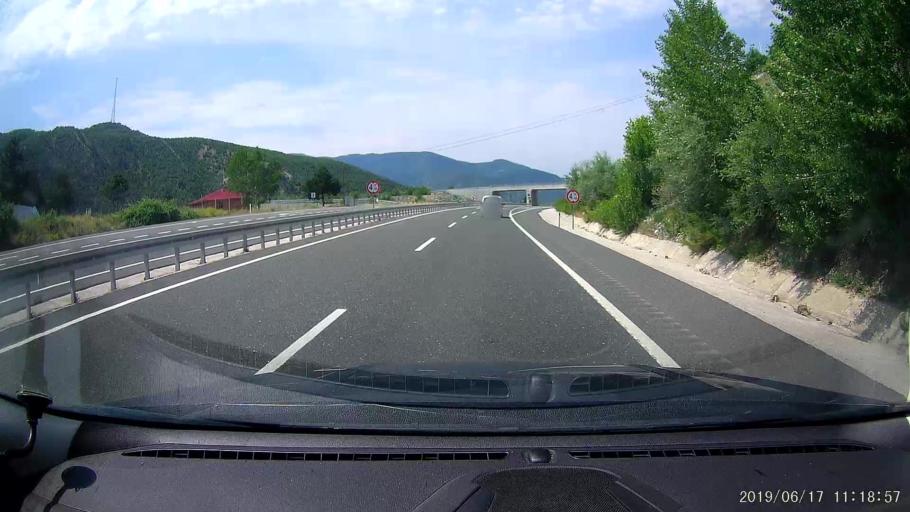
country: TR
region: Cankiri
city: Yaprakli
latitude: 40.9283
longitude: 33.8400
